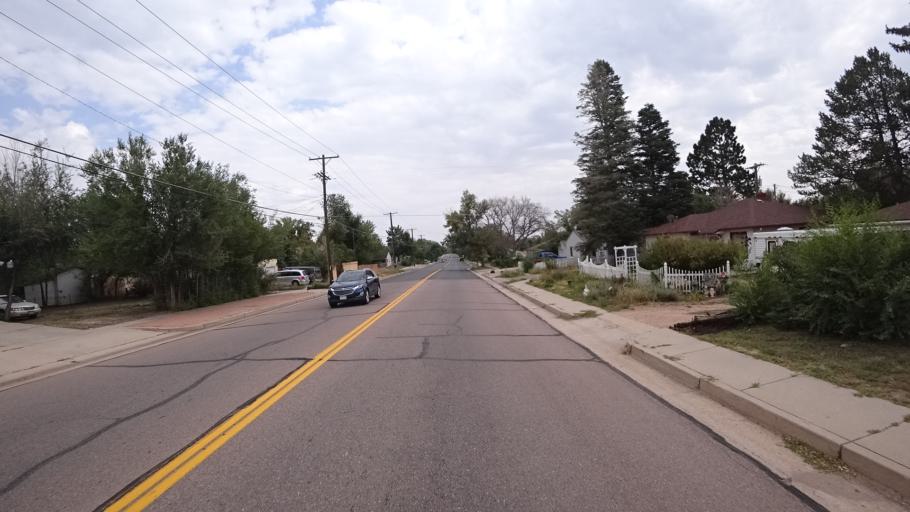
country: US
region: Colorado
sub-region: El Paso County
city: Colorado Springs
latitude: 38.8449
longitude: -104.7898
